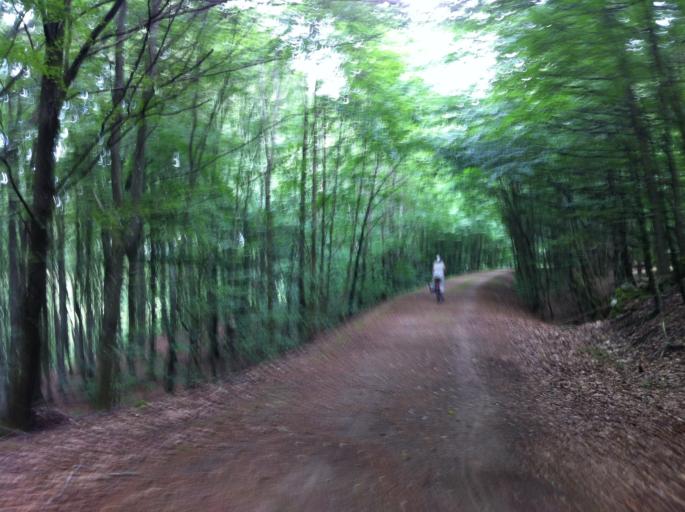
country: SE
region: Skane
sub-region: Hassleholms Kommun
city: Vinslov
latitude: 55.9460
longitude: 13.8622
